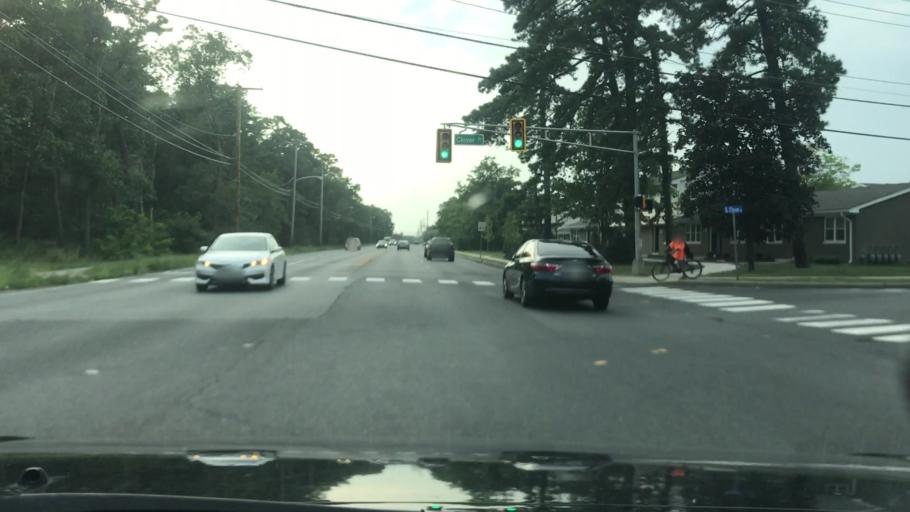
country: US
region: New Jersey
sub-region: Ocean County
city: Lakewood
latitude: 40.0826
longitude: -74.2014
